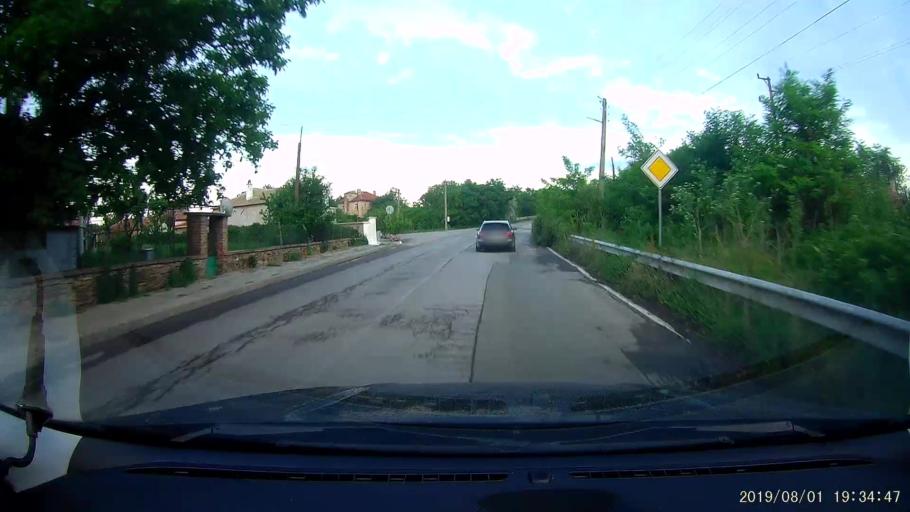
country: BG
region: Burgas
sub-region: Obshtina Sungurlare
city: Sungurlare
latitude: 42.7683
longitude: 26.8782
